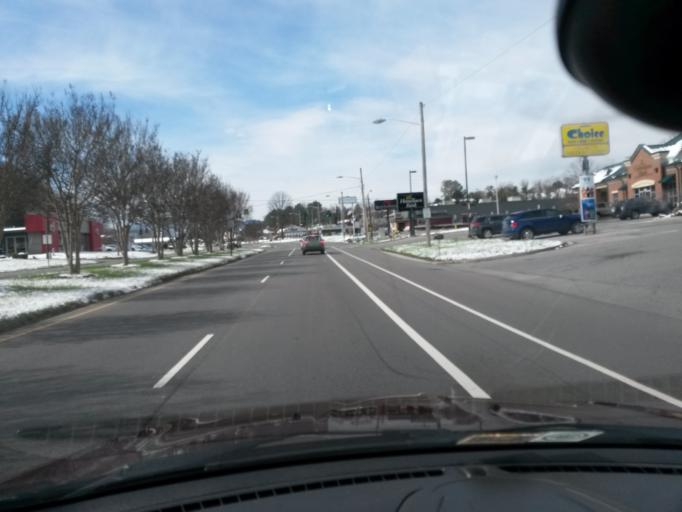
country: US
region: Virginia
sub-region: Roanoke County
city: Narrows
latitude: 37.2381
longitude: -79.9675
